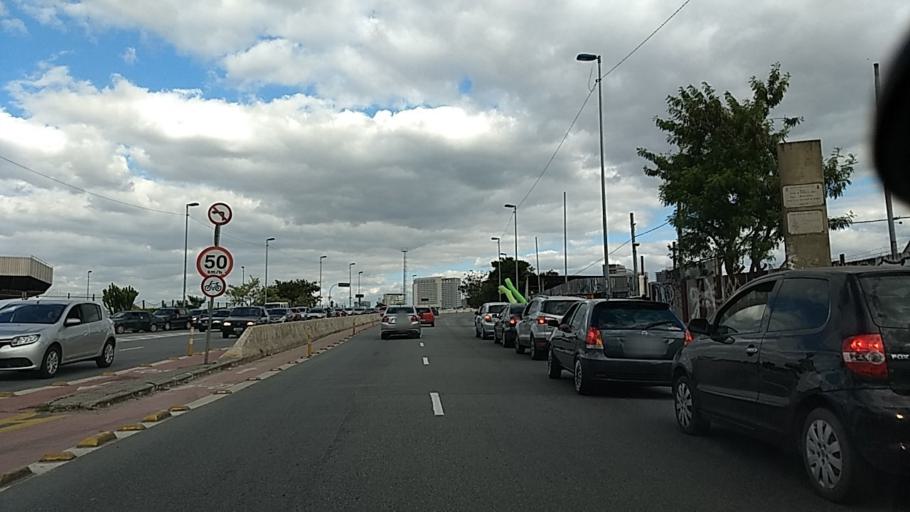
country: BR
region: Sao Paulo
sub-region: Sao Paulo
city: Sao Paulo
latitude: -23.5102
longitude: -46.6792
